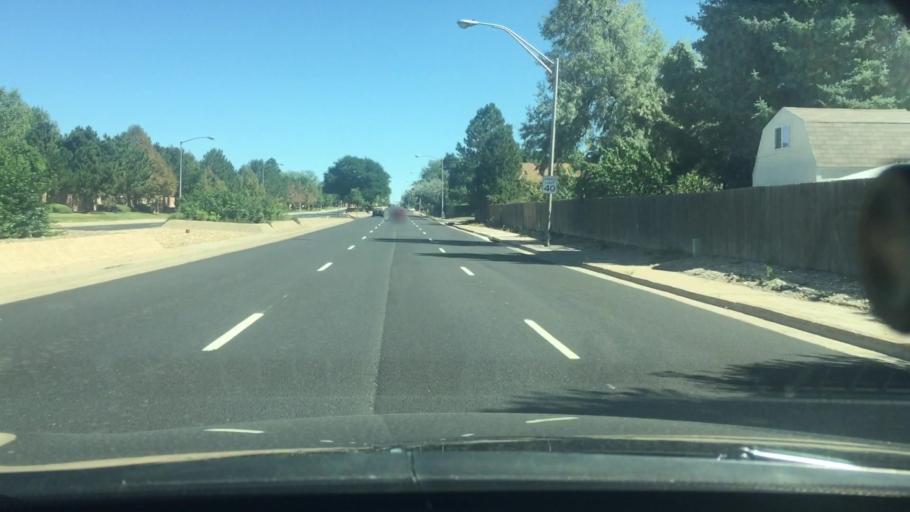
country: US
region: Colorado
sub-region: Arapahoe County
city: Dove Valley
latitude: 39.6385
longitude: -104.8199
